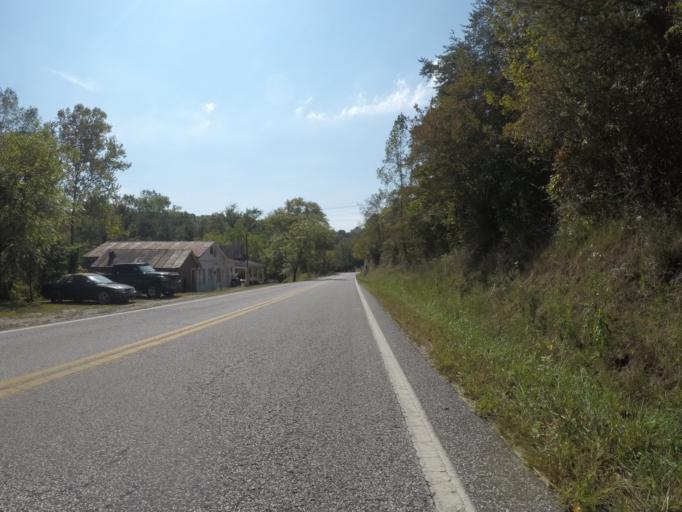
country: US
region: West Virginia
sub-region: Cabell County
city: Lesage
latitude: 38.5527
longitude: -82.3911
